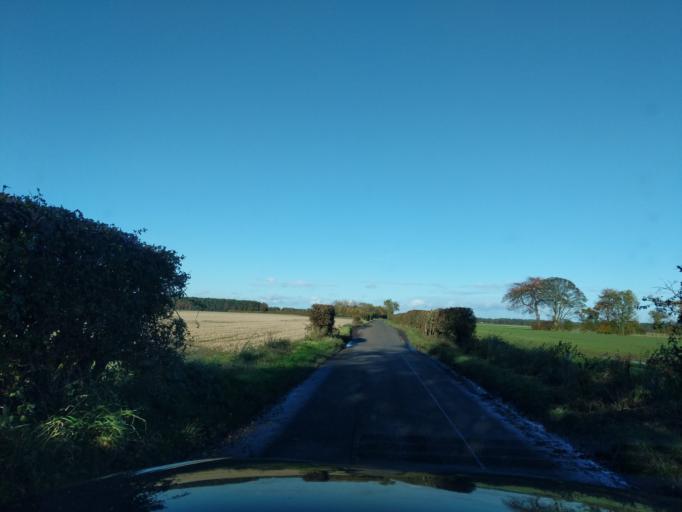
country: GB
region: Scotland
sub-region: Fife
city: Leuchars
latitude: 56.3875
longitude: -2.8765
